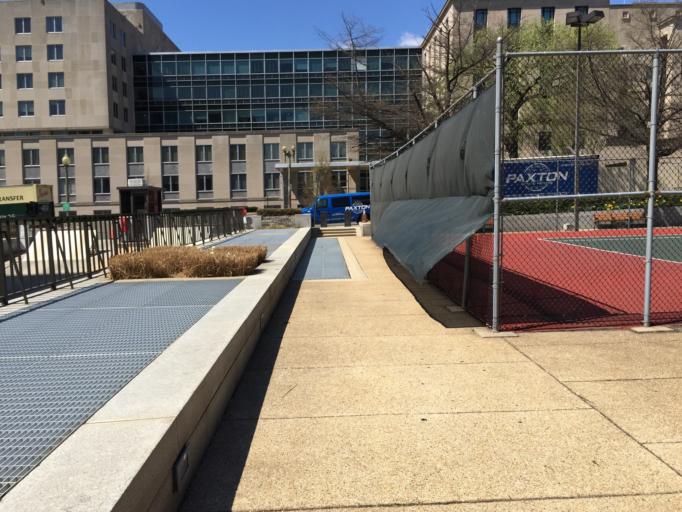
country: US
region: Washington, D.C.
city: Washington, D.C.
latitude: 38.8943
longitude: -77.0462
